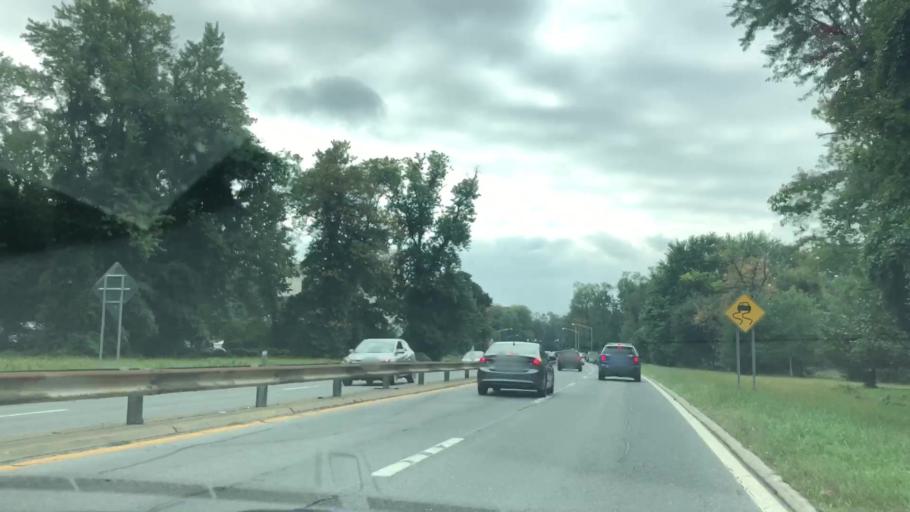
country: US
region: New York
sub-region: Westchester County
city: Hastings-on-Hudson
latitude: 40.9770
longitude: -73.8685
